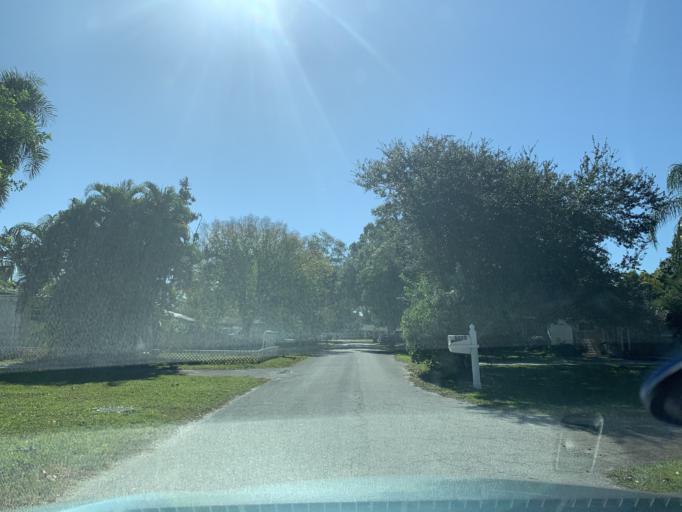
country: US
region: Florida
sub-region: Pinellas County
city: Kenneth City
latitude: 27.8112
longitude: -82.7473
